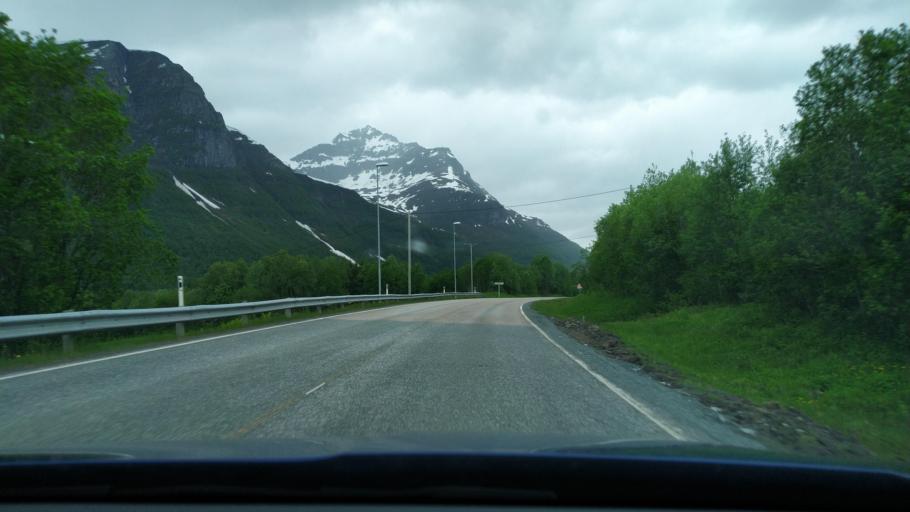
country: NO
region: Troms
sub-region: Balsfjord
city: Storsteinnes
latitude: 69.3778
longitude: 19.2858
